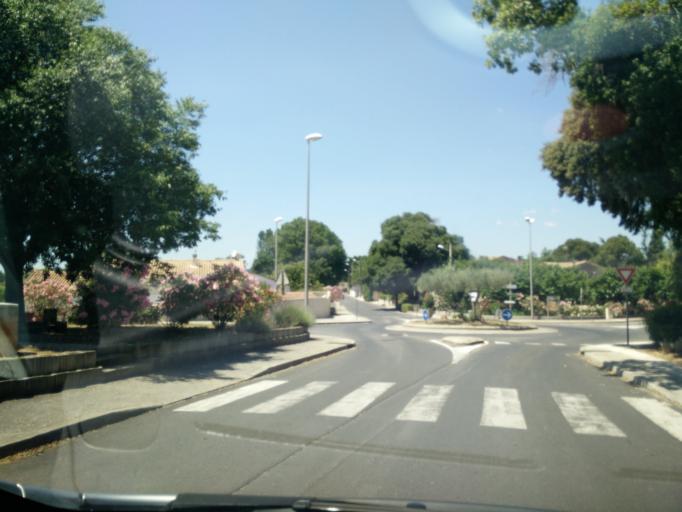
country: FR
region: Languedoc-Roussillon
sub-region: Departement de l'Herault
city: Saint-Christol
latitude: 43.7175
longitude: 4.0986
